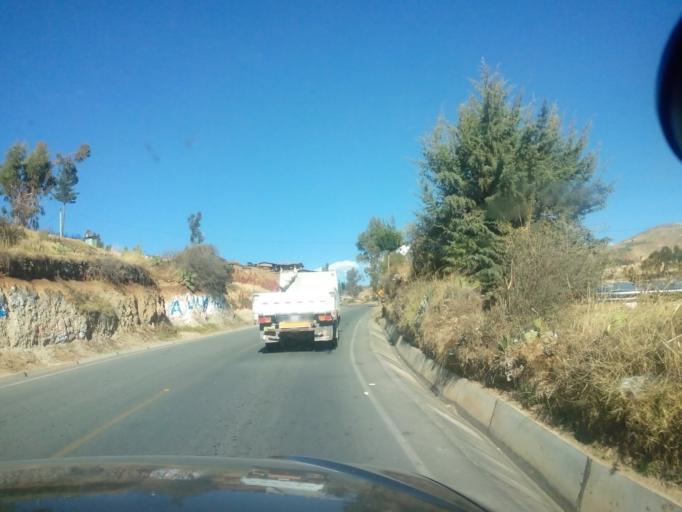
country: PE
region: Apurimac
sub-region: Provincia de Andahuaylas
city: San Jeronimo
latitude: -13.6455
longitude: -73.3312
